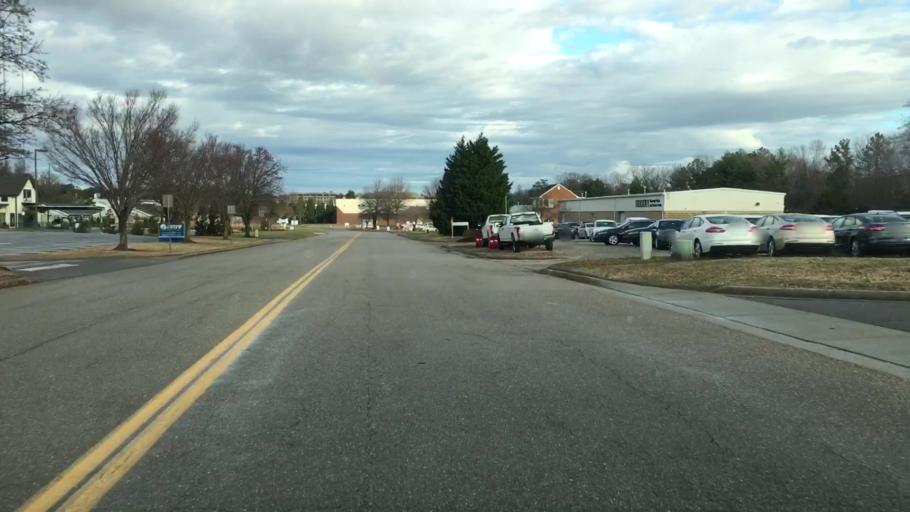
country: US
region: Virginia
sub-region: Chesterfield County
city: Bon Air
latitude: 37.5009
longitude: -77.5911
